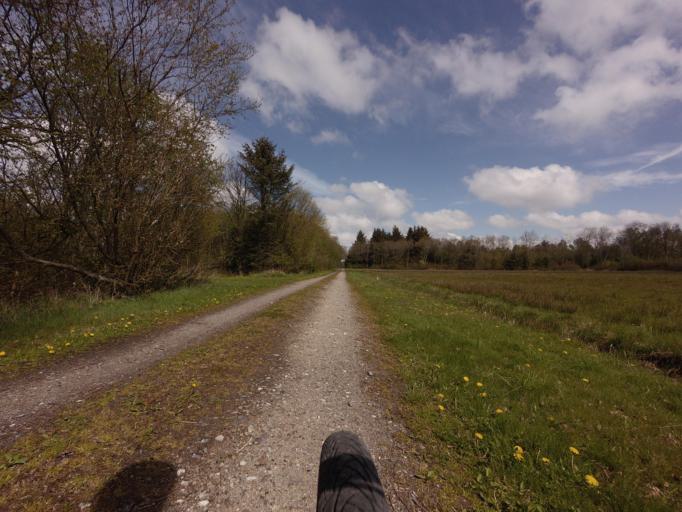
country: DK
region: North Denmark
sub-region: Jammerbugt Kommune
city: Kas
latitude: 57.1925
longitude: 9.5936
